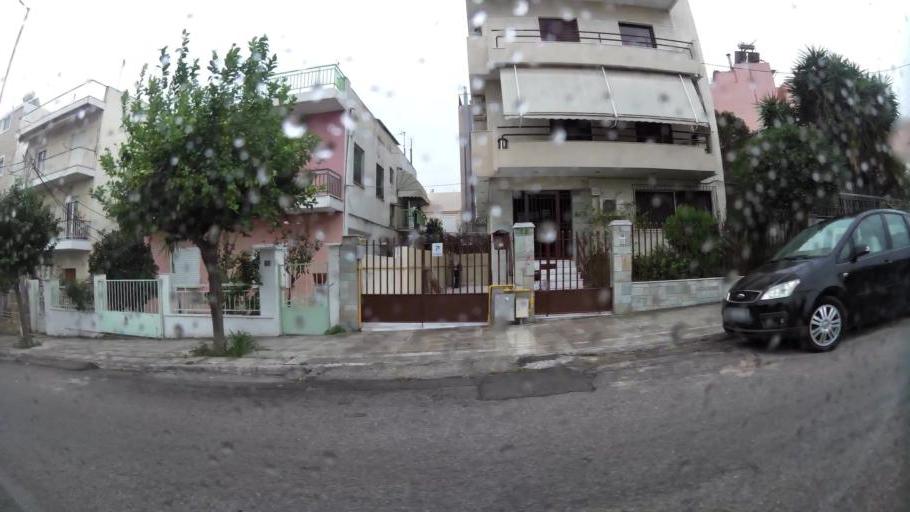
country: GR
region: Attica
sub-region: Nomarchia Athinas
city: Peristeri
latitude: 38.0167
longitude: 23.6963
